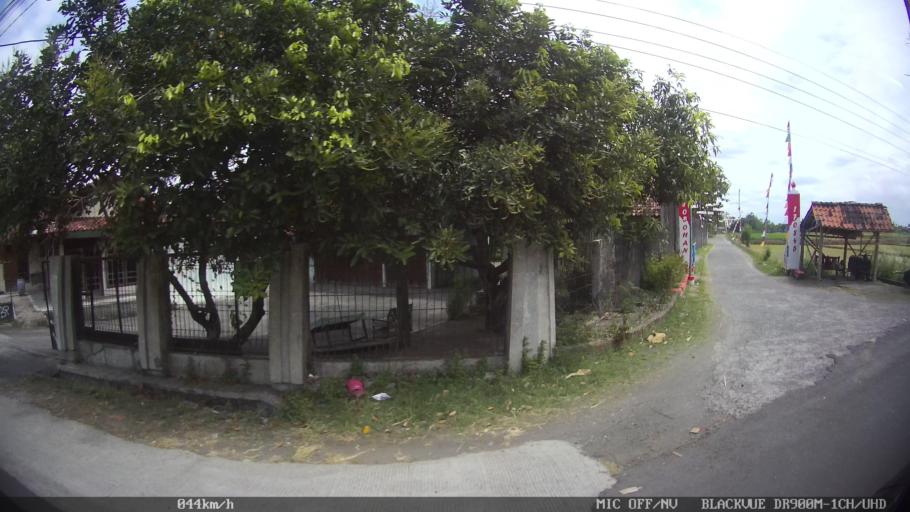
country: ID
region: Central Java
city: Candi Prambanan
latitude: -7.7755
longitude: 110.4822
